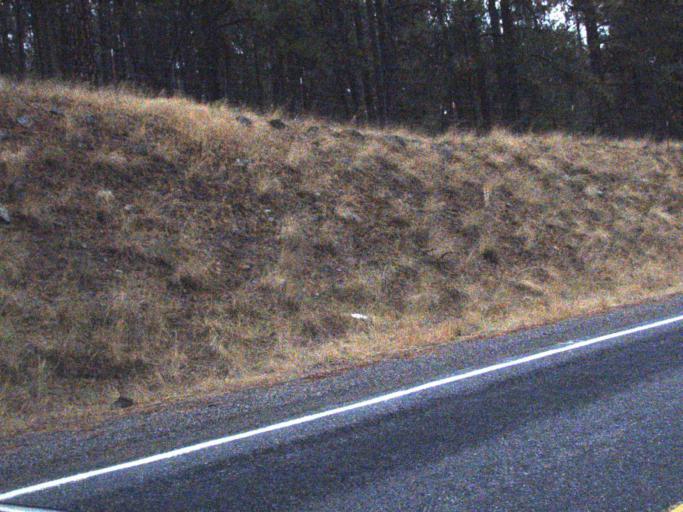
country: US
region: Washington
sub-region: Spokane County
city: Fairchild Air Force Base
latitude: 47.8405
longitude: -117.8522
